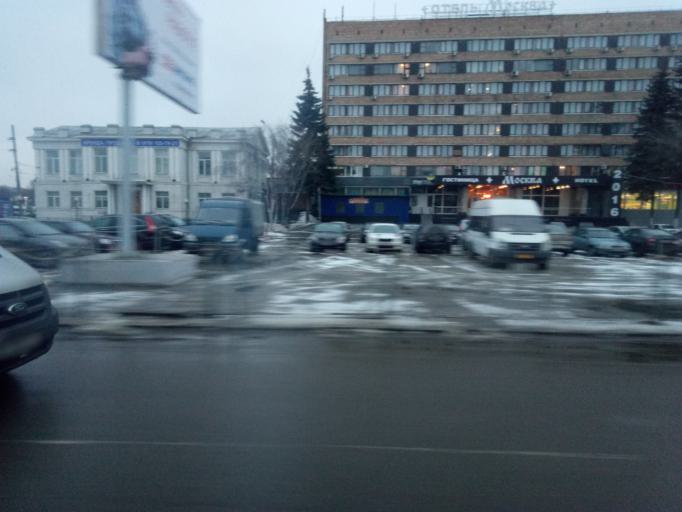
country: RU
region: Tula
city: Tula
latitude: 54.1988
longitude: 37.5785
